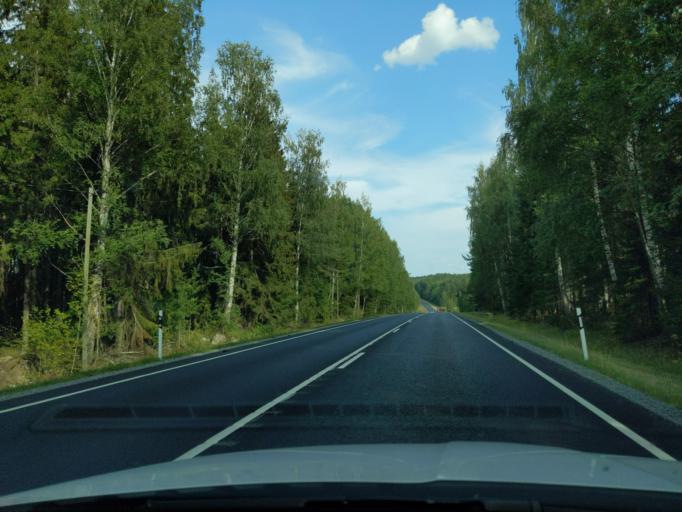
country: FI
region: Haeme
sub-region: Haemeenlinna
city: Tuulos
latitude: 61.1578
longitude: 24.6969
